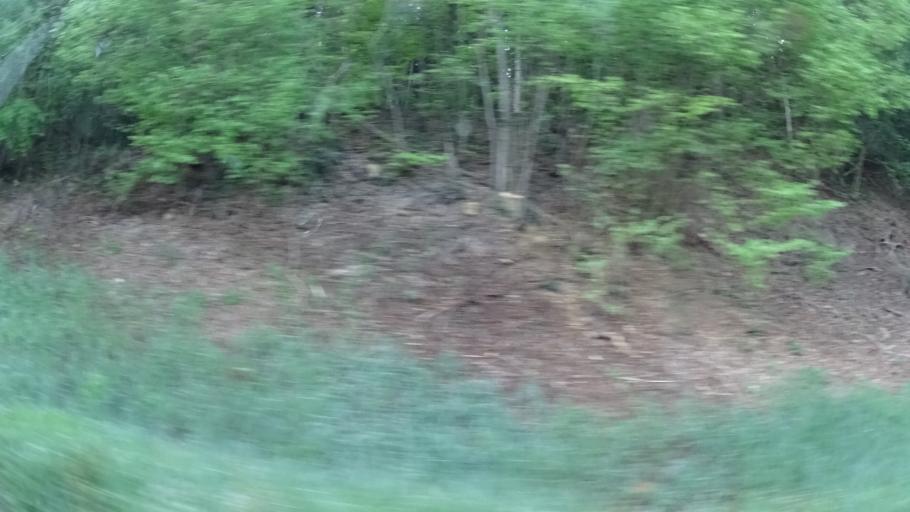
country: DE
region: Baden-Wuerttemberg
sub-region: Tuebingen Region
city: Haigerloch
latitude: 48.4130
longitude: 8.7689
